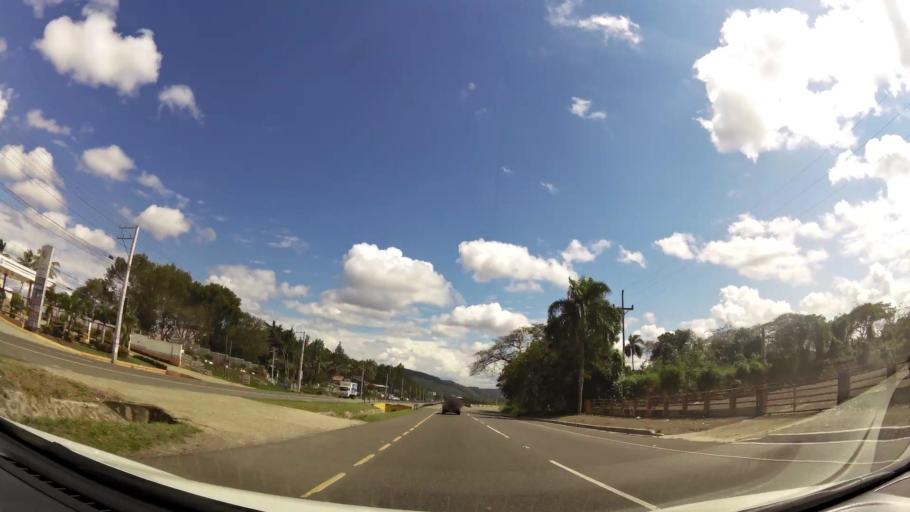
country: DO
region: La Vega
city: Rio Verde Arriba
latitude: 19.3302
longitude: -70.5929
